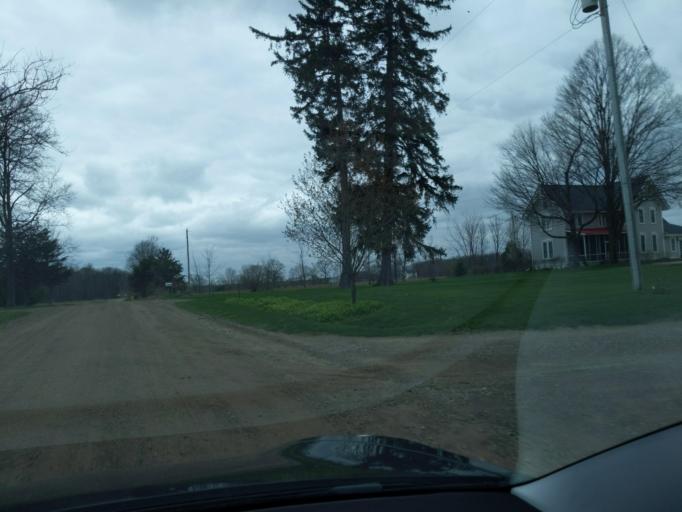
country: US
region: Michigan
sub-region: Ingham County
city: Stockbridge
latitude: 42.4465
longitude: -84.1461
